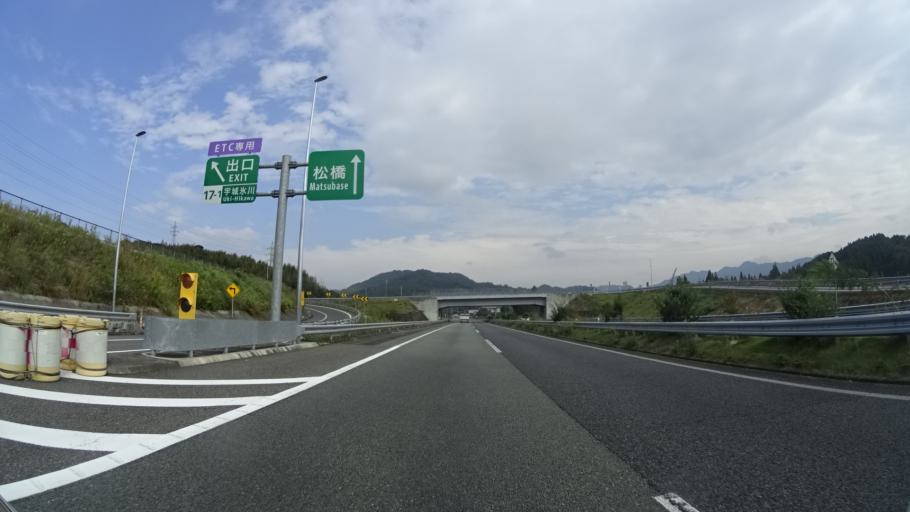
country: JP
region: Kumamoto
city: Matsubase
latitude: 32.5763
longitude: 130.7095
